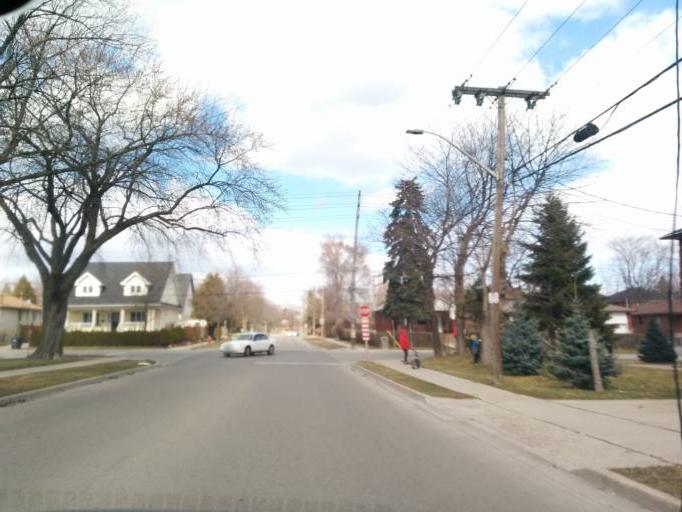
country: CA
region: Ontario
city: Etobicoke
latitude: 43.5814
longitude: -79.5658
